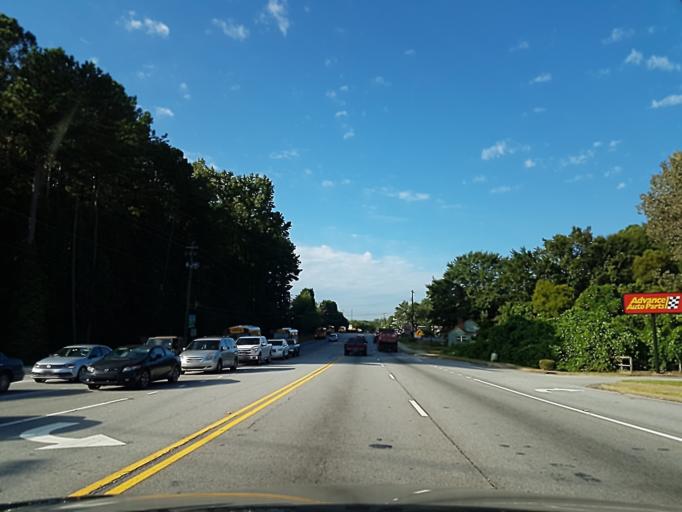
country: US
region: Georgia
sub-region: Gwinnett County
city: Lilburn
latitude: 33.8929
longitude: -84.1416
